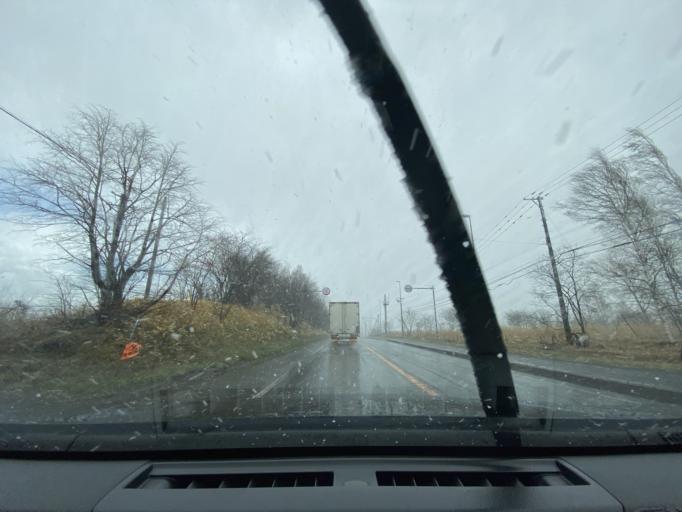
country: JP
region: Hokkaido
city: Fukagawa
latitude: 43.6476
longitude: 141.9620
